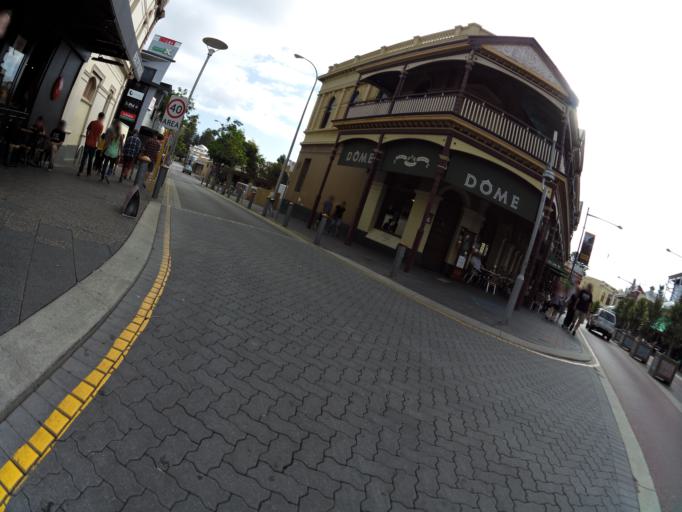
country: AU
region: Western Australia
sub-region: Fremantle
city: South Fremantle
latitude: -32.0558
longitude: 115.7476
